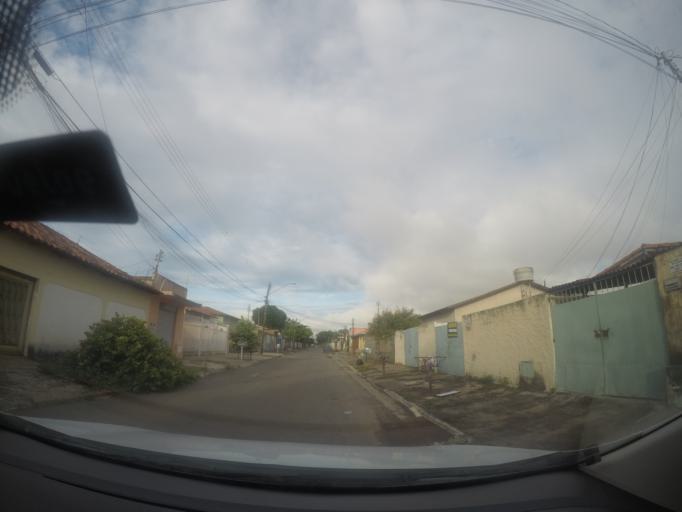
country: BR
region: Goias
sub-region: Goiania
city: Goiania
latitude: -16.6851
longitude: -49.3113
